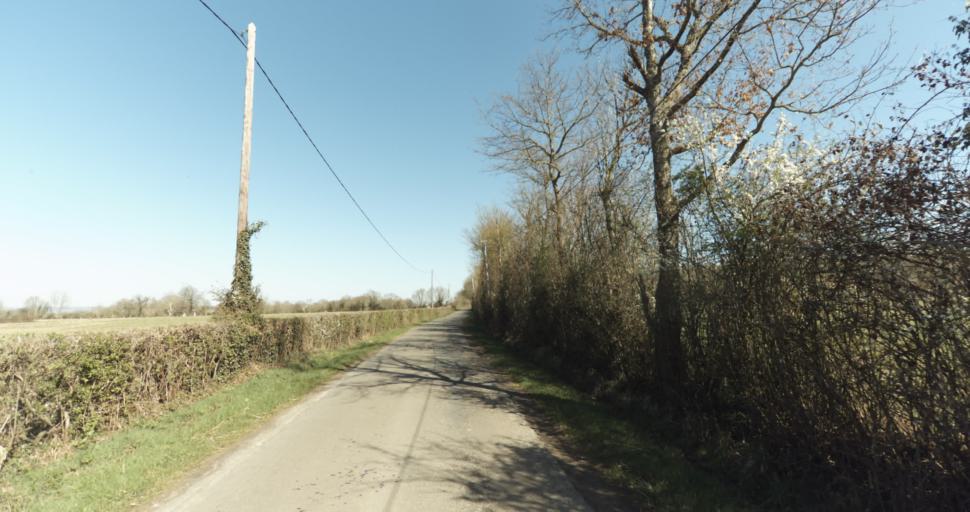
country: FR
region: Lower Normandy
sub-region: Departement du Calvados
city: Livarot
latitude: 49.0223
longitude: 0.0910
